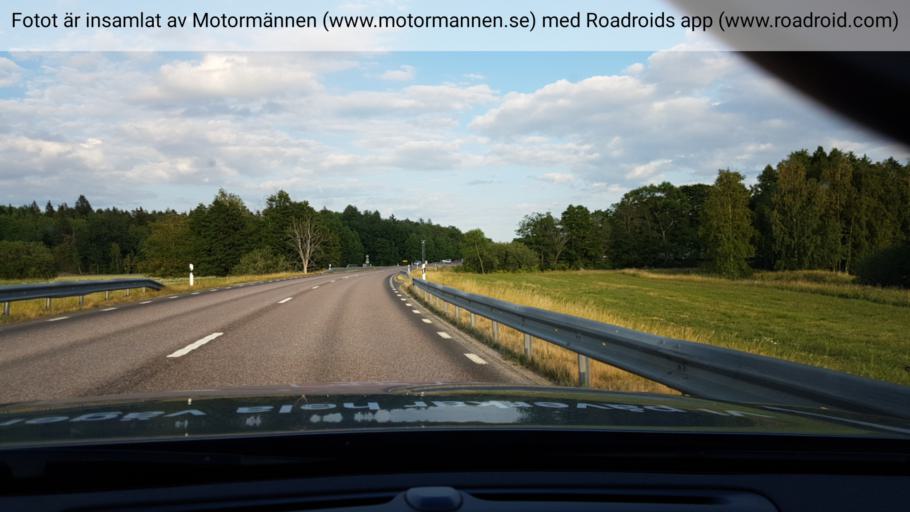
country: SE
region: Uppsala
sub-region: Enkopings Kommun
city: Orsundsbro
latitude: 59.8786
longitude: 17.2819
